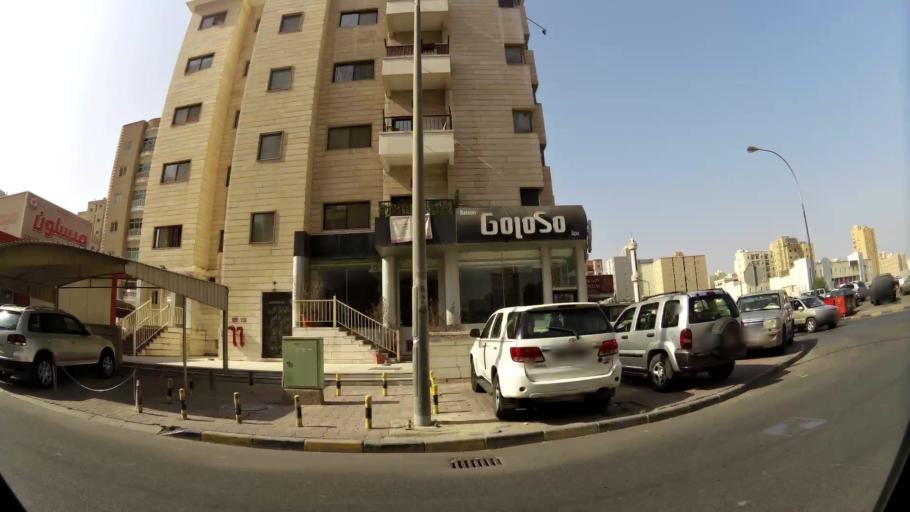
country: KW
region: Muhafazat Hawalli
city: Hawalli
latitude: 29.3293
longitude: 48.0170
